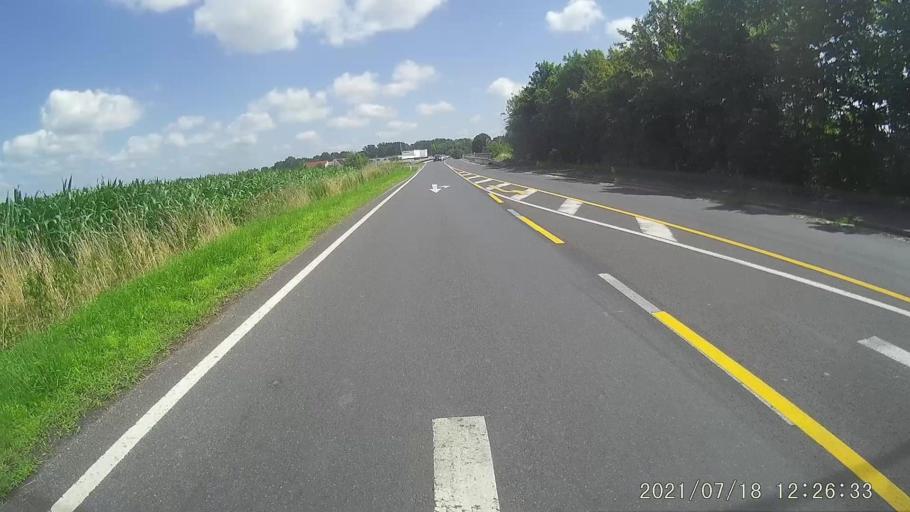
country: DE
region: Saxony
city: Goerlitz
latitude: 51.1632
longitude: 14.9557
